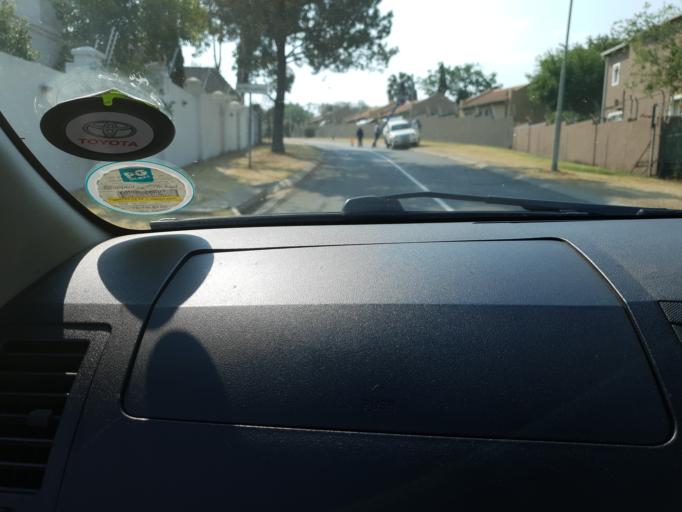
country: ZA
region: Gauteng
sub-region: City of Johannesburg Metropolitan Municipality
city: Midrand
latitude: -25.9924
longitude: 28.1106
